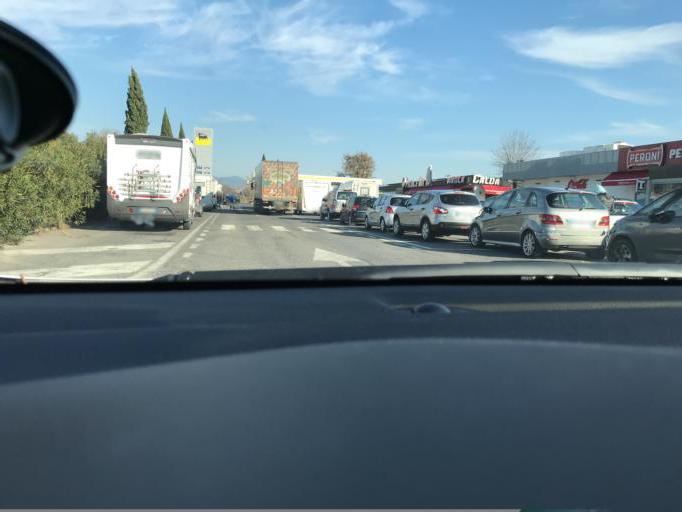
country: IT
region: Latium
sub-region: Provincia di Viterbo
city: Orte Scalo
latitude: 42.4599
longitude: 12.4177
